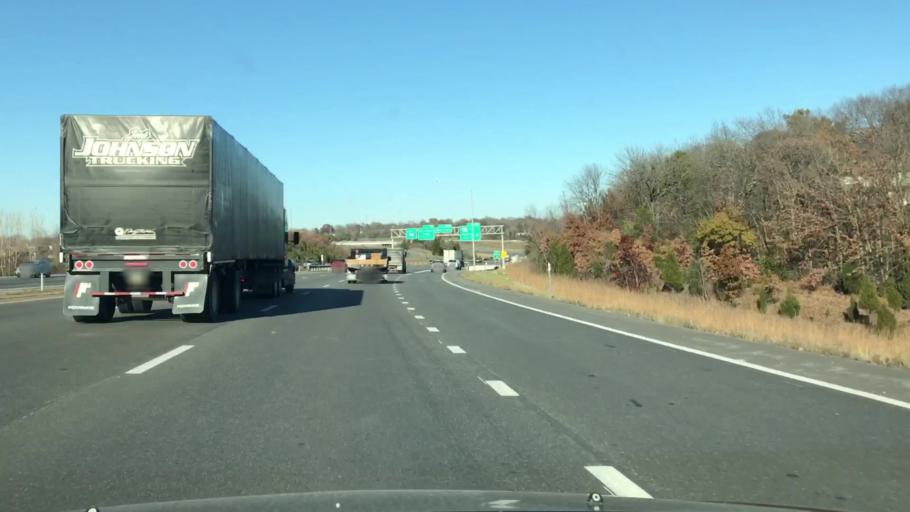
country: US
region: Missouri
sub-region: Jackson County
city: Raytown
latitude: 39.0069
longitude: -94.5012
